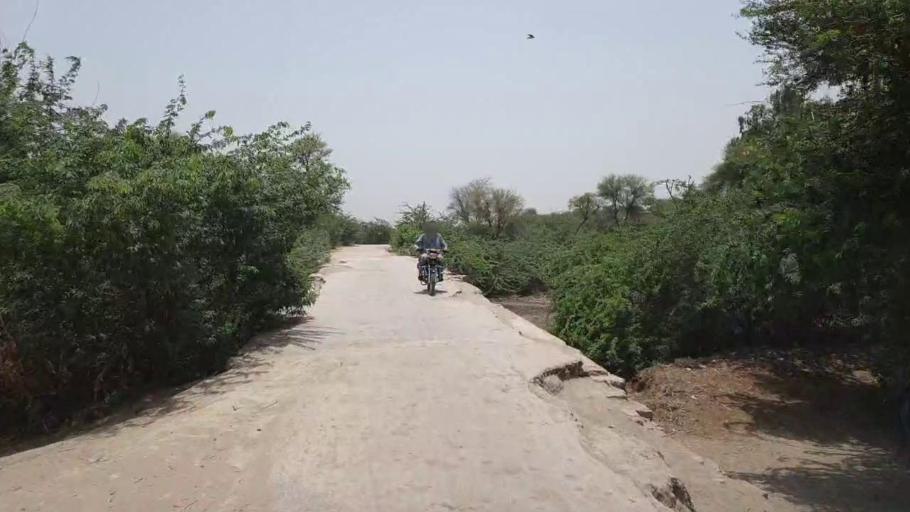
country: PK
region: Sindh
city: Tando Mittha Khan
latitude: 26.0602
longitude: 69.1985
